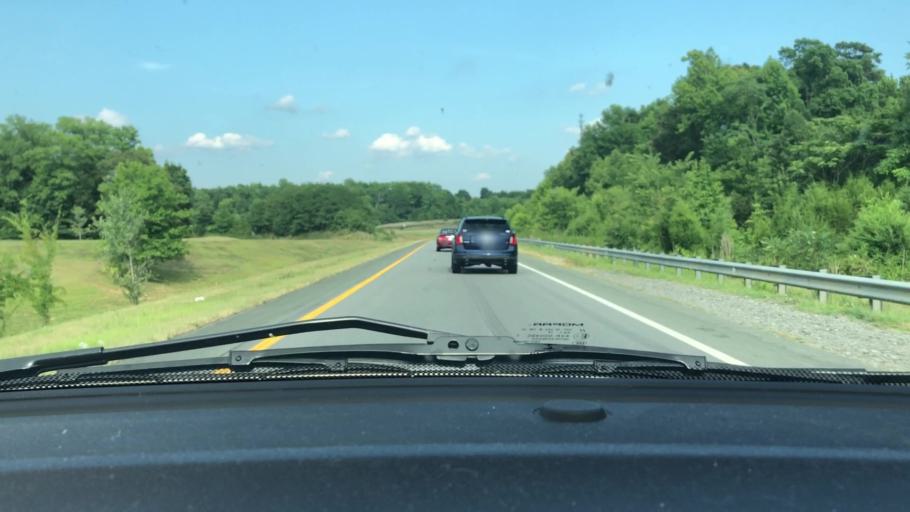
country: US
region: North Carolina
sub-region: Guilford County
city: Pleasant Garden
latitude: 35.9968
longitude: -79.7539
